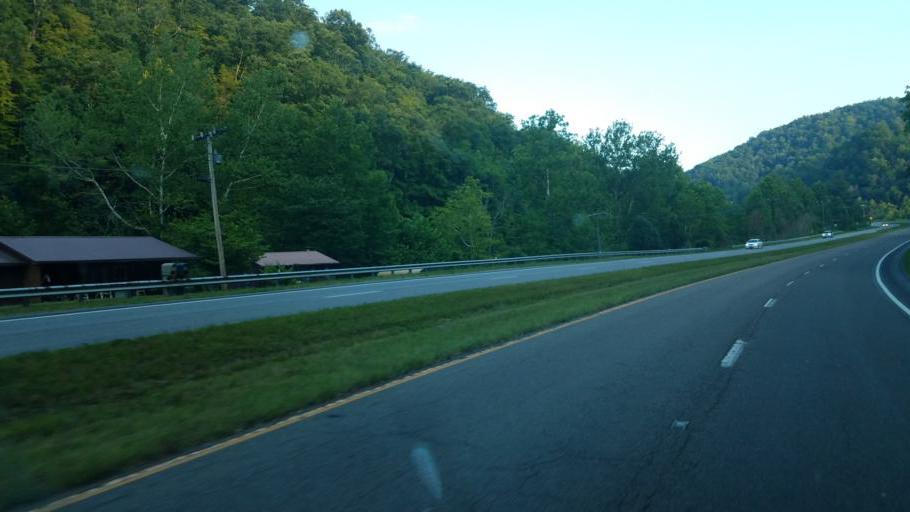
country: US
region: Tennessee
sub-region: Hawkins County
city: Church Hill
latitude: 36.6790
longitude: -82.7554
